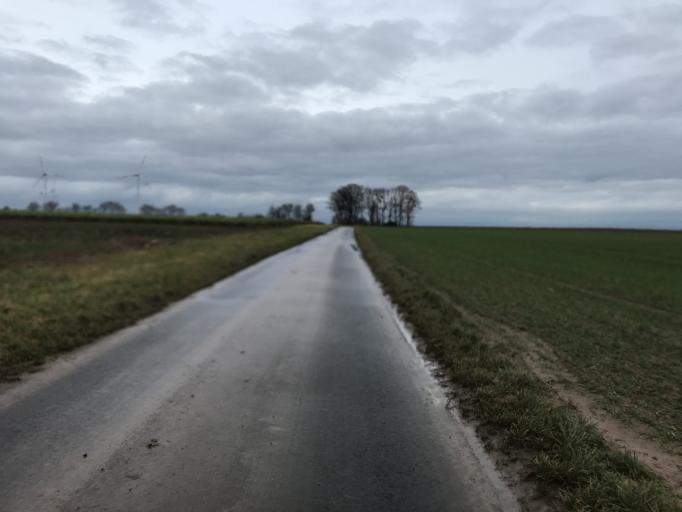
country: DE
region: Rheinland-Pfalz
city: Gau-Bischofsheim
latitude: 49.9282
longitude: 8.2493
